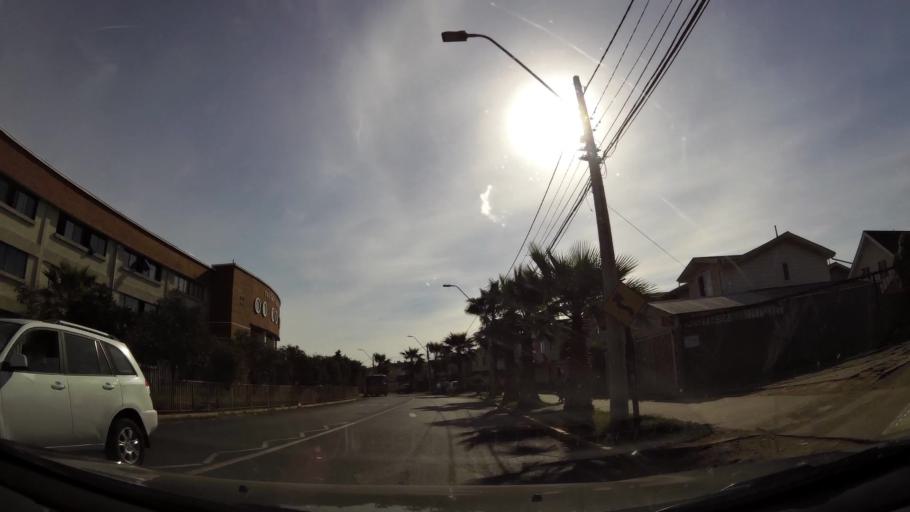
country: CL
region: Santiago Metropolitan
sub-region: Provincia de Cordillera
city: Puente Alto
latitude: -33.5923
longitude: -70.5581
